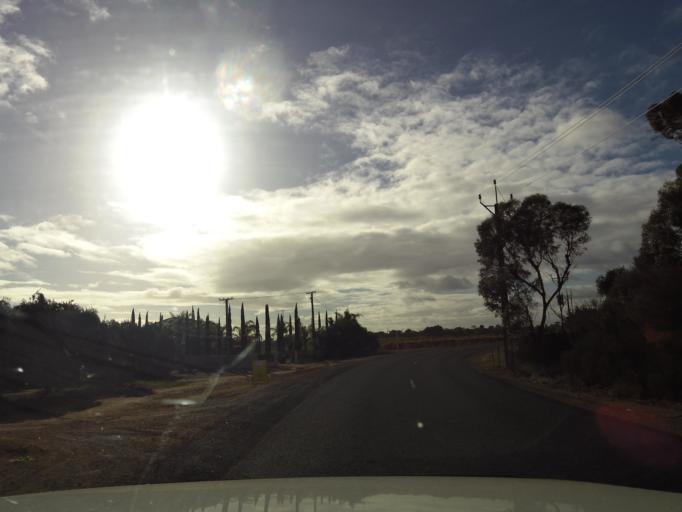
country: AU
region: South Australia
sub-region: Berri and Barmera
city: Berri
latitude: -34.2685
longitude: 140.5941
